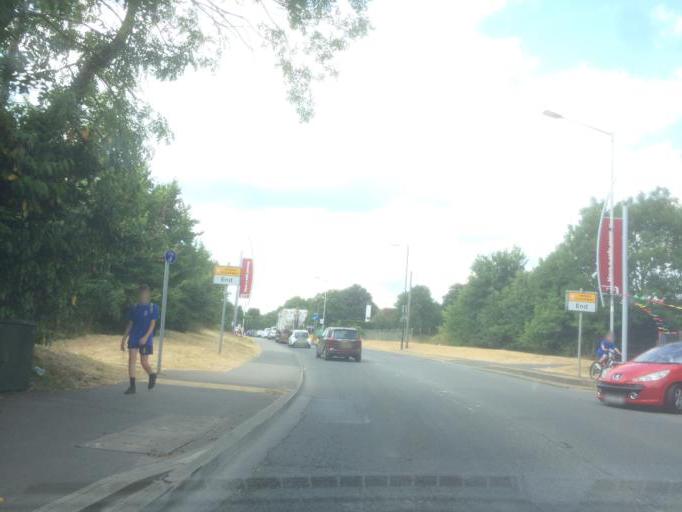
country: GB
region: England
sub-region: Buckinghamshire
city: Farnham Royal
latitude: 51.5335
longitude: -0.6175
